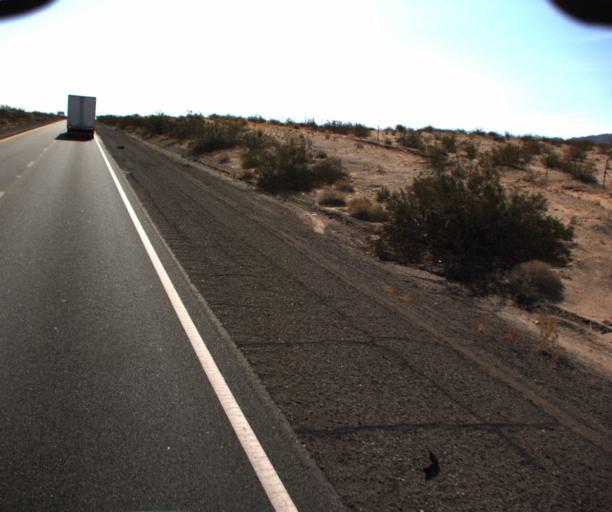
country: US
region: Arizona
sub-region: Mohave County
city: Desert Hills
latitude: 34.7202
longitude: -114.4504
